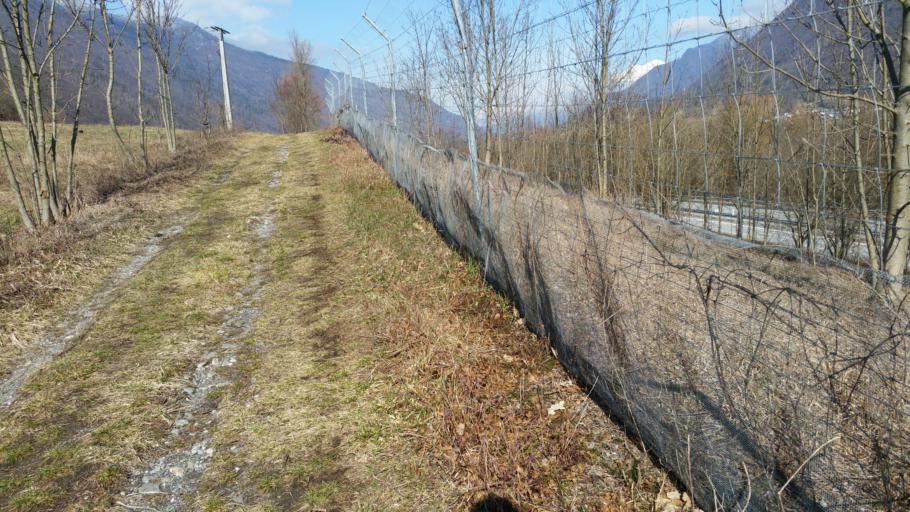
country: FR
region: Rhone-Alpes
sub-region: Departement de la Savoie
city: Saint-Remy-de-Maurienne
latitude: 45.4013
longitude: 6.2723
